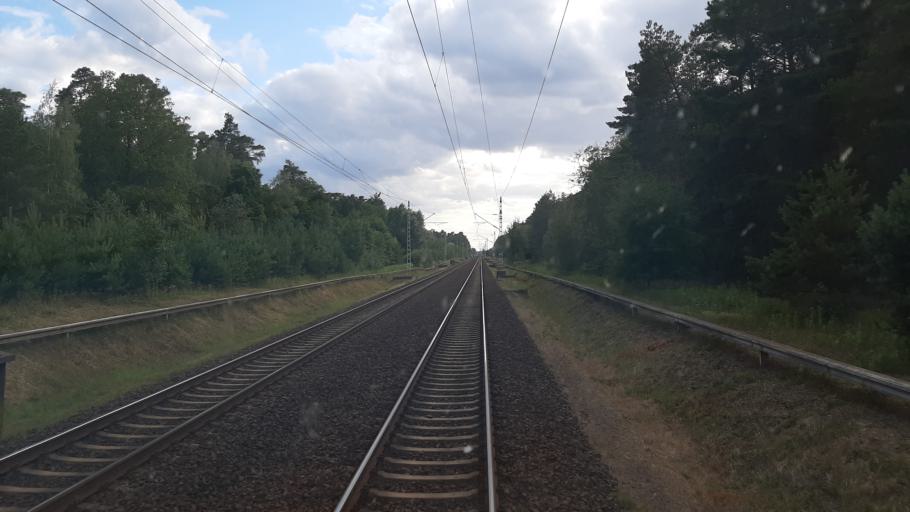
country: DE
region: Brandenburg
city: Falkensee
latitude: 52.6241
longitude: 13.1096
